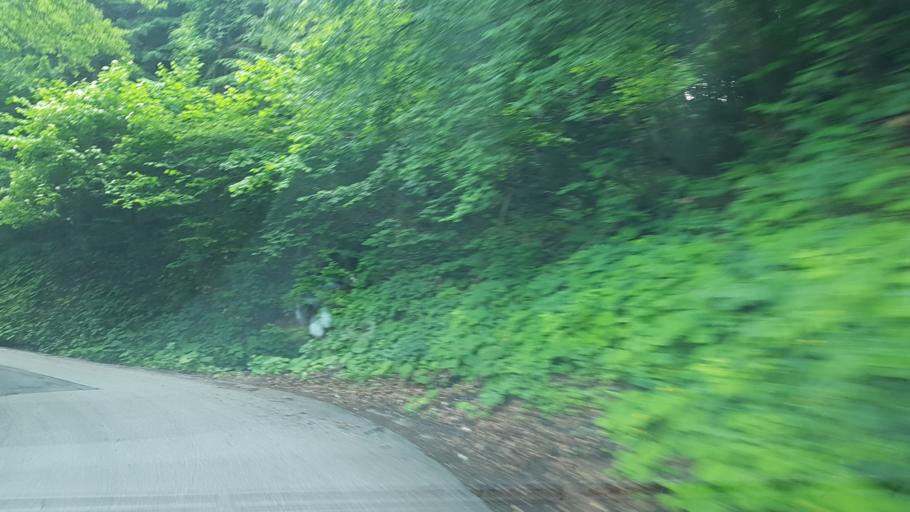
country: SI
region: Dobrna
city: Dobrna
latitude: 46.3848
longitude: 15.1796
